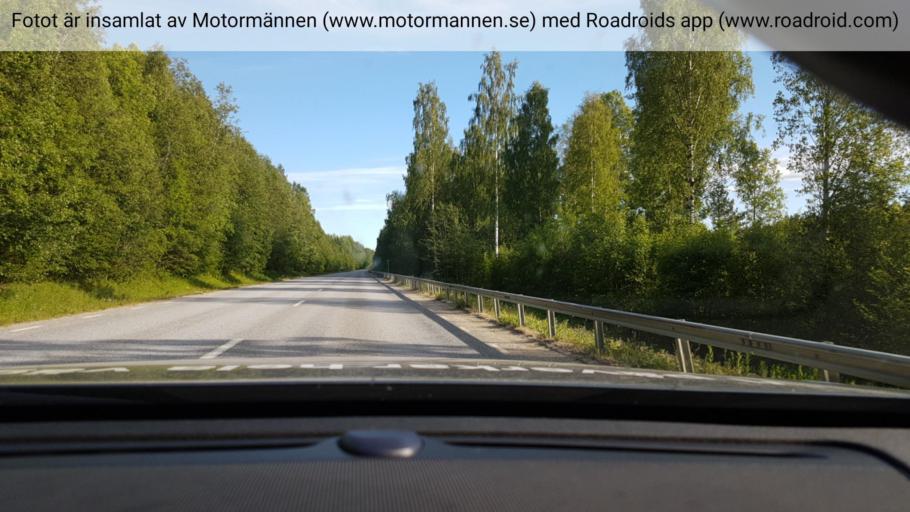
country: SE
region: Vaesterbotten
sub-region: Vindelns Kommun
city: Vindeln
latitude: 64.3032
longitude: 19.6146
